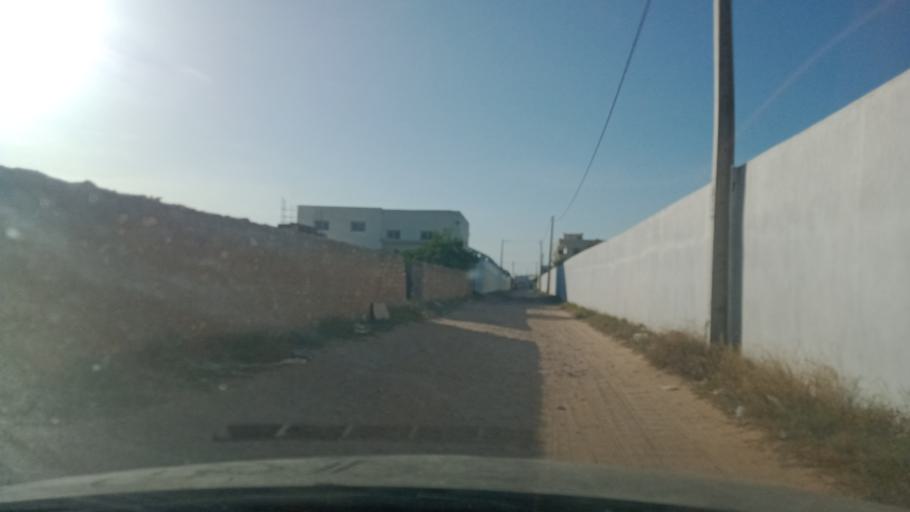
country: TN
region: Safaqis
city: Sfax
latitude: 34.8159
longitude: 10.7399
